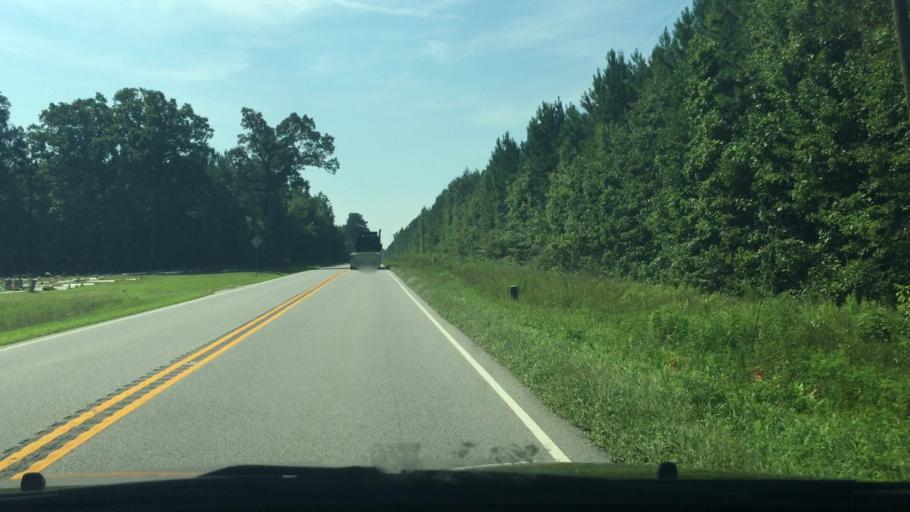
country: US
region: Virginia
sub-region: Sussex County
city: Sussex
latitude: 36.8685
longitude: -77.1418
